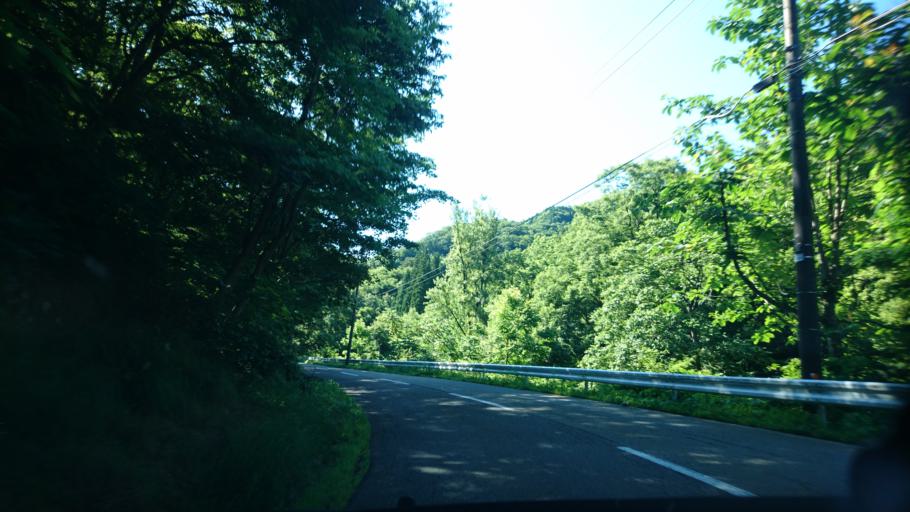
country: JP
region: Akita
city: Kakunodatemachi
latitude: 39.7136
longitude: 140.6270
